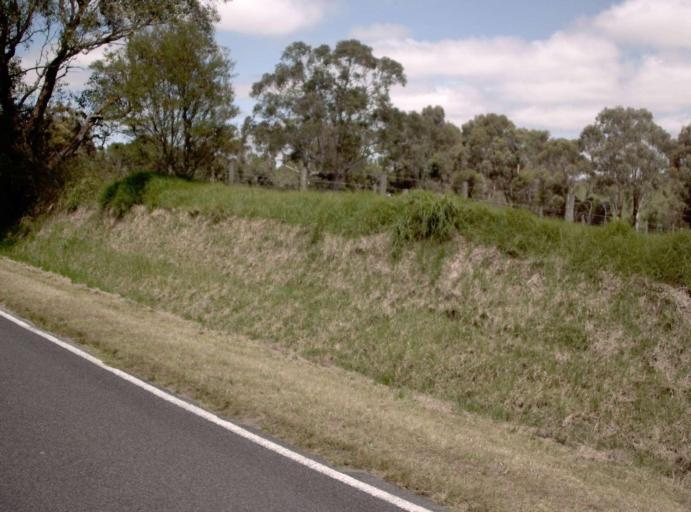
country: AU
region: Victoria
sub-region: Bass Coast
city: North Wonthaggi
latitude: -38.5826
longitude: 146.0228
